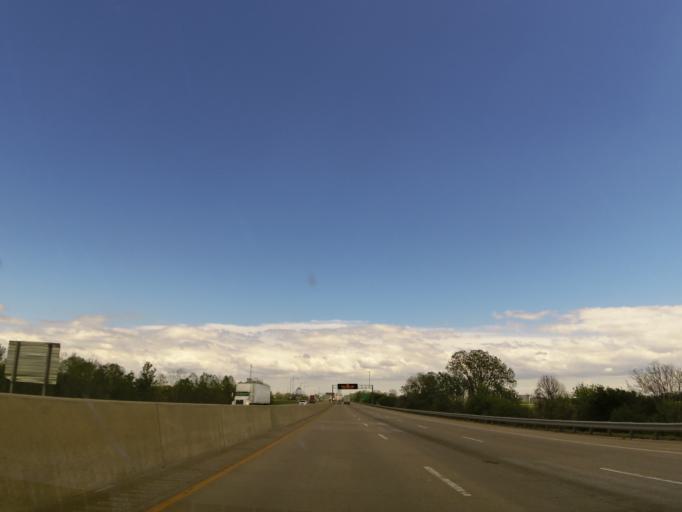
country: US
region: Tennessee
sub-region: Shelby County
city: Memphis
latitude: 35.1530
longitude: -90.0953
